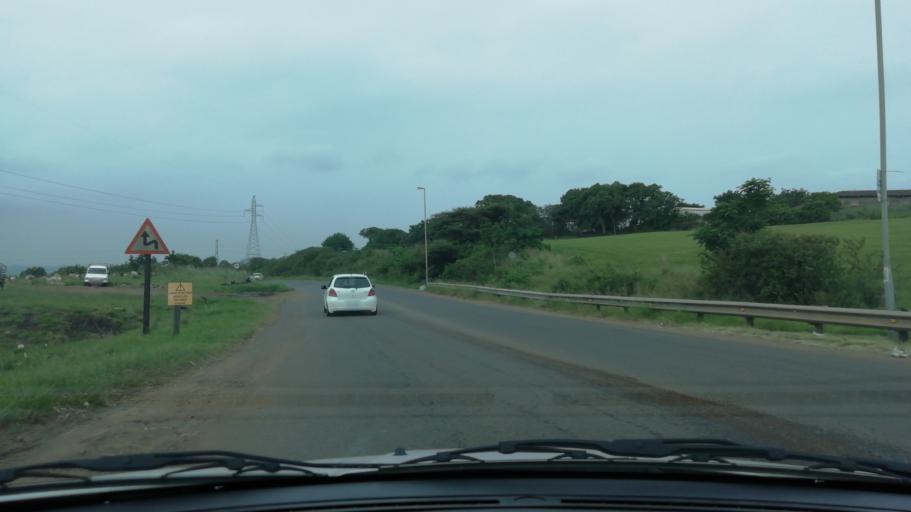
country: ZA
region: KwaZulu-Natal
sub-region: uThungulu District Municipality
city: Empangeni
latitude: -28.7415
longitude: 31.8824
